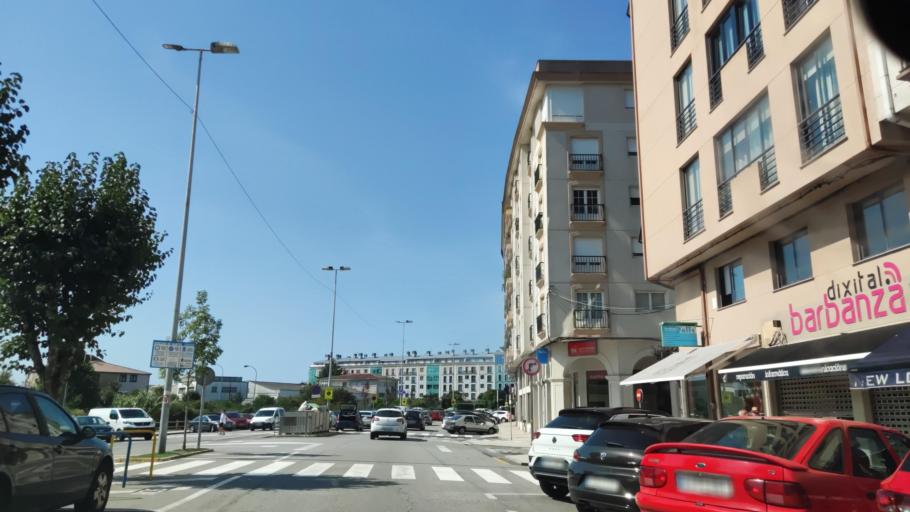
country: ES
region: Galicia
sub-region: Provincia da Coruna
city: Boiro
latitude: 42.6472
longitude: -8.8795
